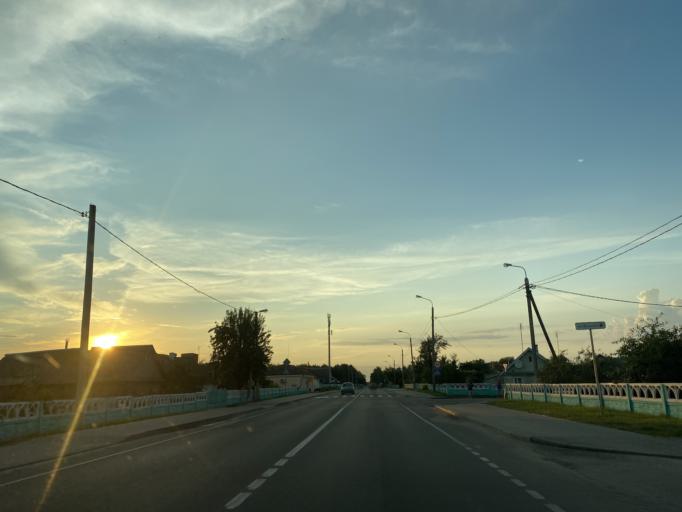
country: BY
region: Brest
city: Ivatsevichy
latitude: 52.7100
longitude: 25.3531
